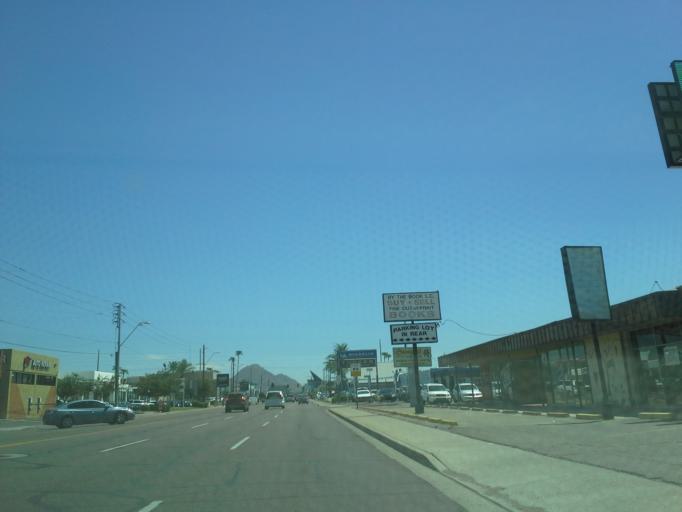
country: US
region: Arizona
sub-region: Maricopa County
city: Phoenix
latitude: 33.5092
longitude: -112.0592
